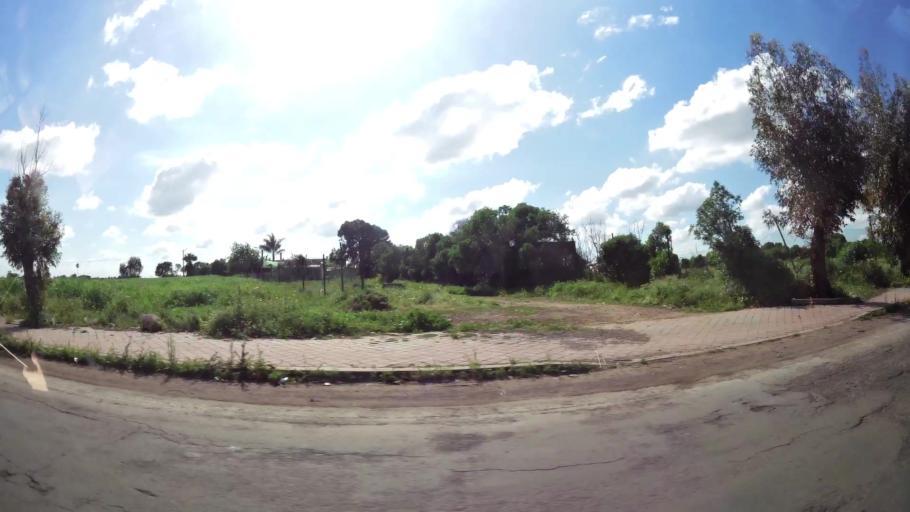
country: MA
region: Grand Casablanca
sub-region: Mediouna
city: Mediouna
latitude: 33.4467
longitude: -7.5210
